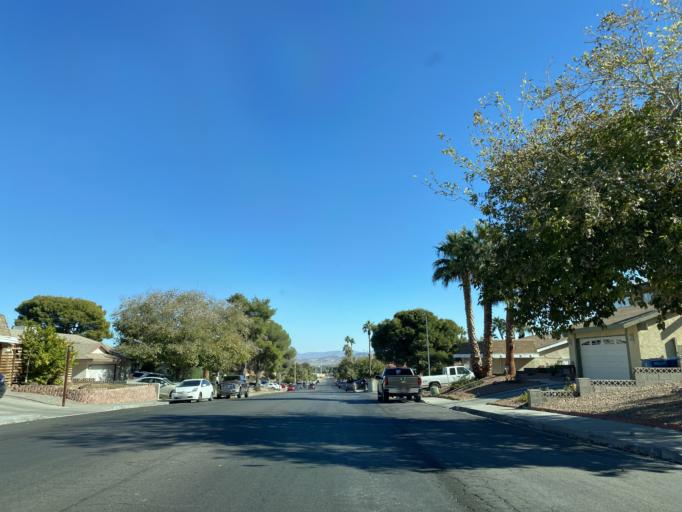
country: US
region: Nevada
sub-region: Clark County
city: Whitney
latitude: 36.0967
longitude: -115.0878
